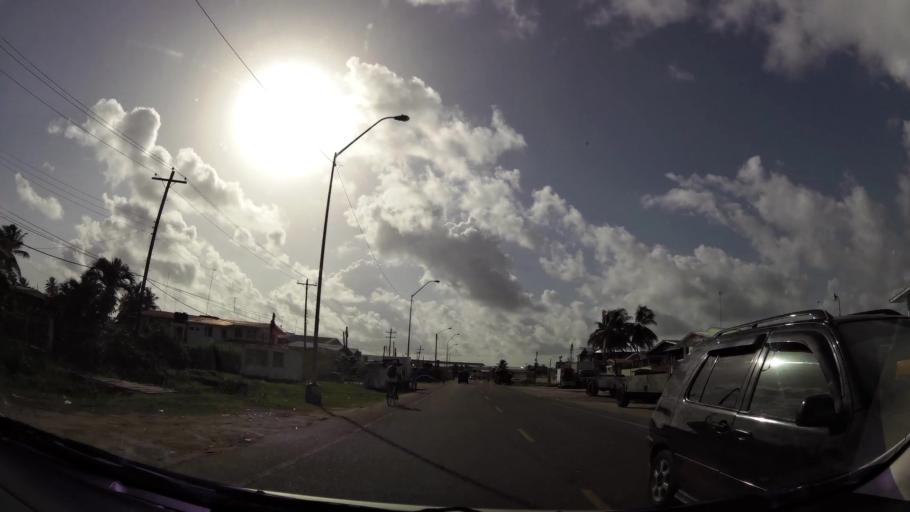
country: GY
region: Demerara-Mahaica
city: Georgetown
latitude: 6.8177
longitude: -58.0850
